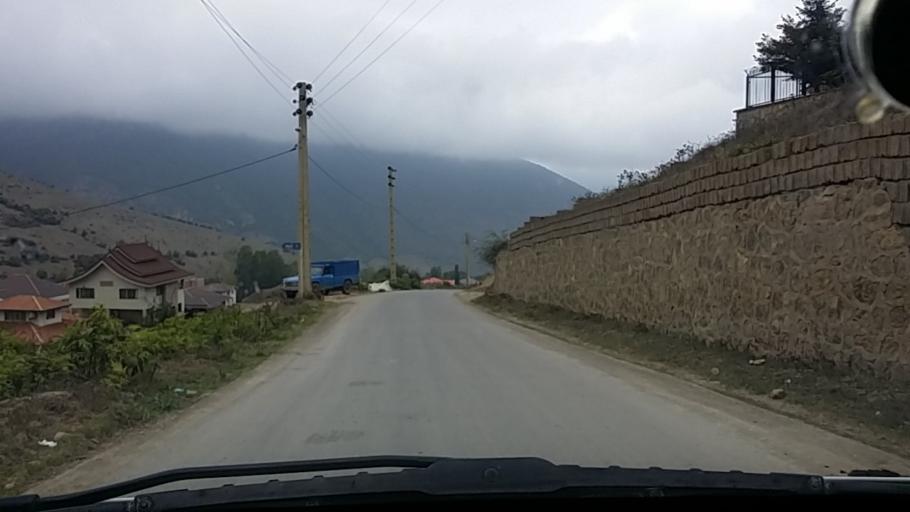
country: IR
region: Mazandaran
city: `Abbasabad
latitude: 36.4741
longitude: 51.1403
